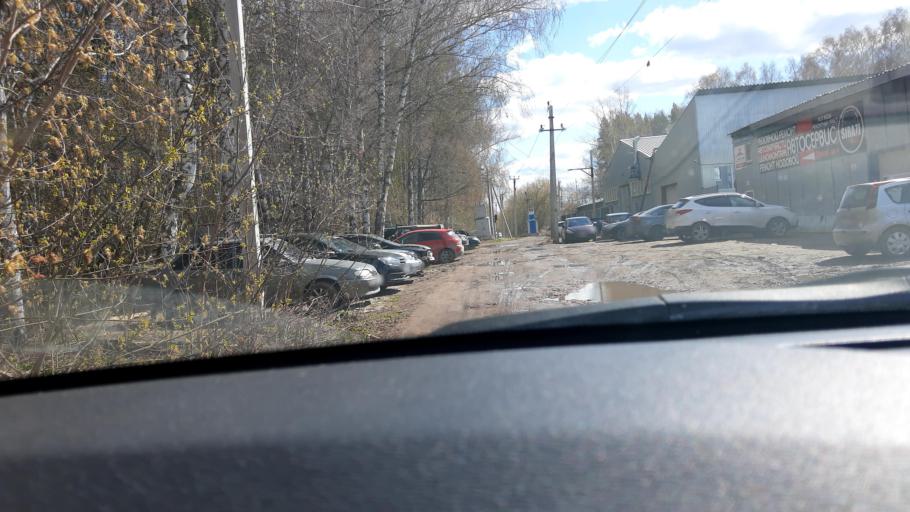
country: RU
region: Bashkortostan
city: Ufa
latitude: 54.6963
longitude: 55.9350
